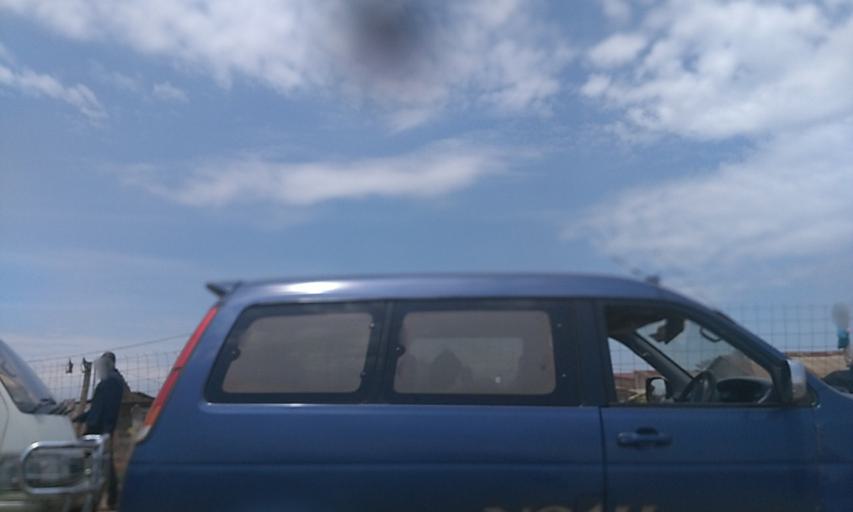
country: UG
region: Central Region
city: Kampala Central Division
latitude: 0.3529
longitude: 32.5734
